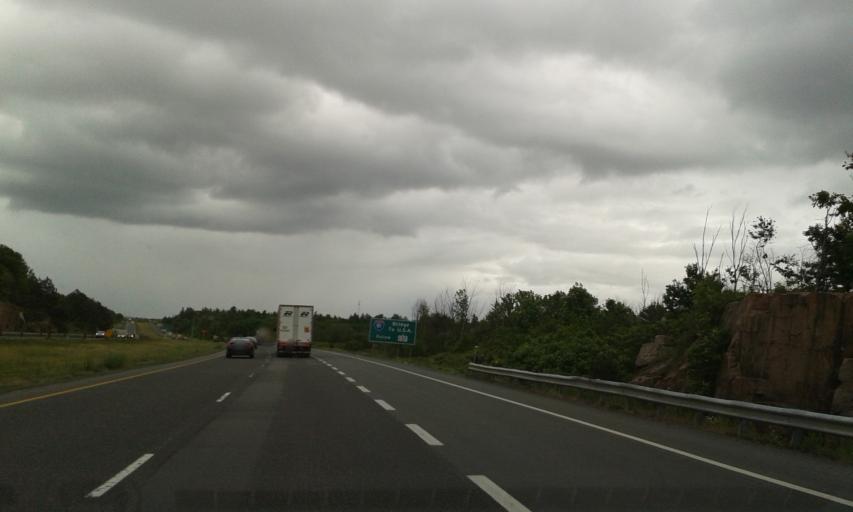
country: US
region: New York
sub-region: Jefferson County
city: Alexandria Bay
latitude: 44.3776
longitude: -76.0038
